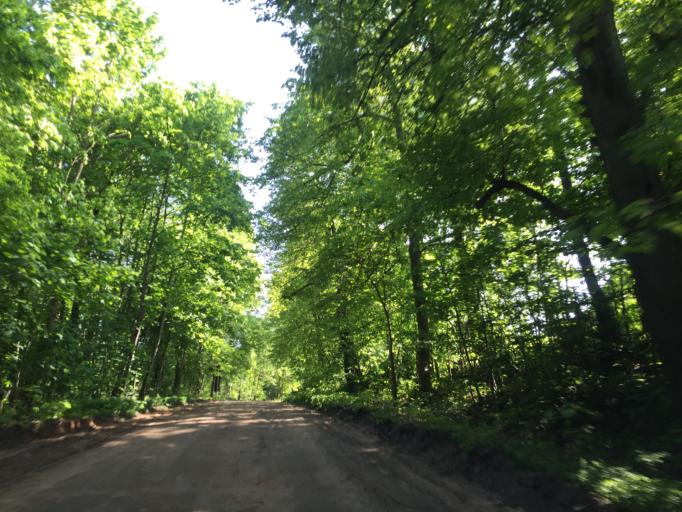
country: LV
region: Ikskile
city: Ikskile
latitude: 56.8262
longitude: 24.4300
